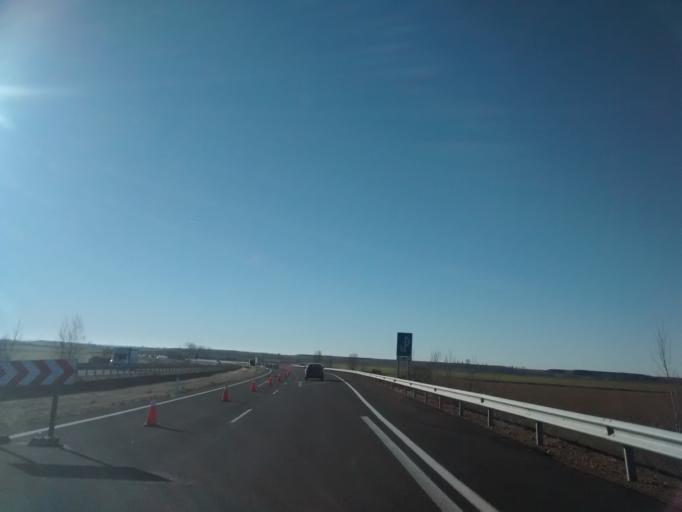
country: ES
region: Castille and Leon
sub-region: Provincia de Palencia
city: Abia de las Torres
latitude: 42.4429
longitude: -4.3955
